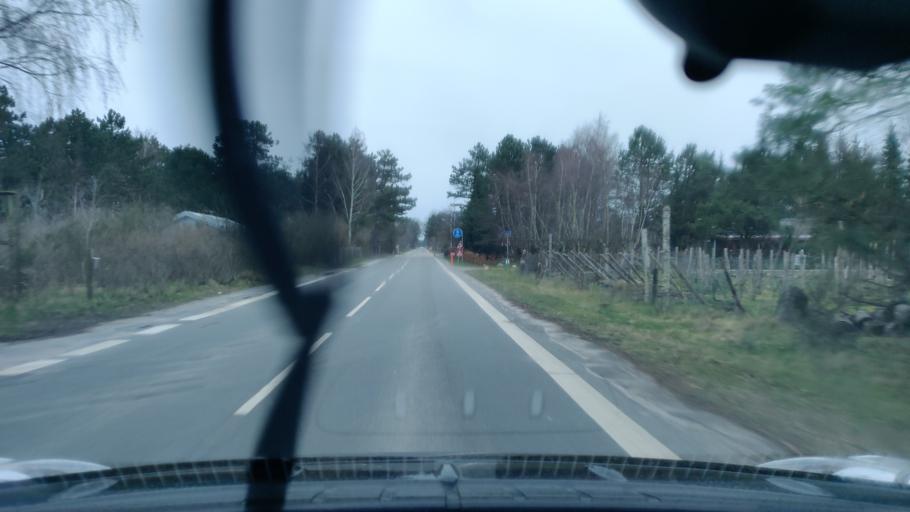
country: DK
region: Zealand
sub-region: Odsherred Kommune
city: Hojby
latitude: 55.8732
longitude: 11.5412
